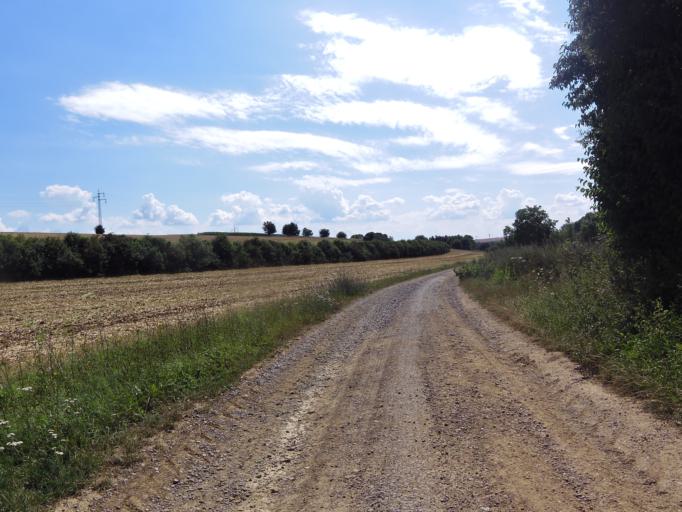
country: DE
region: Bavaria
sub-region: Regierungsbezirk Unterfranken
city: Estenfeld
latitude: 49.8303
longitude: 9.9836
